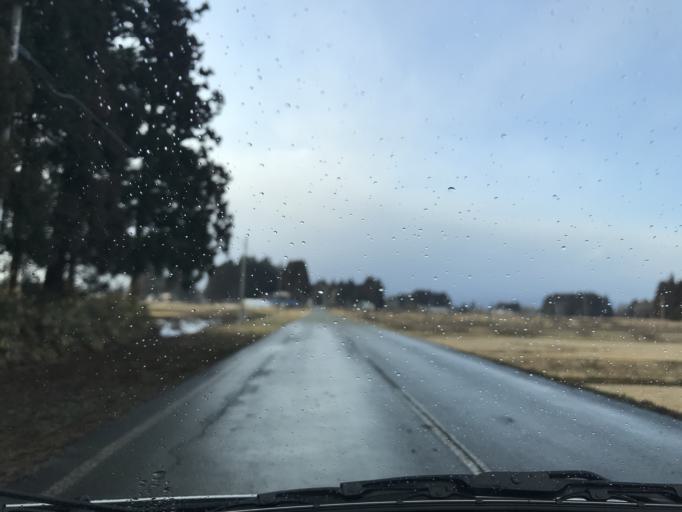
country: JP
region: Iwate
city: Mizusawa
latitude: 39.0934
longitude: 141.0288
